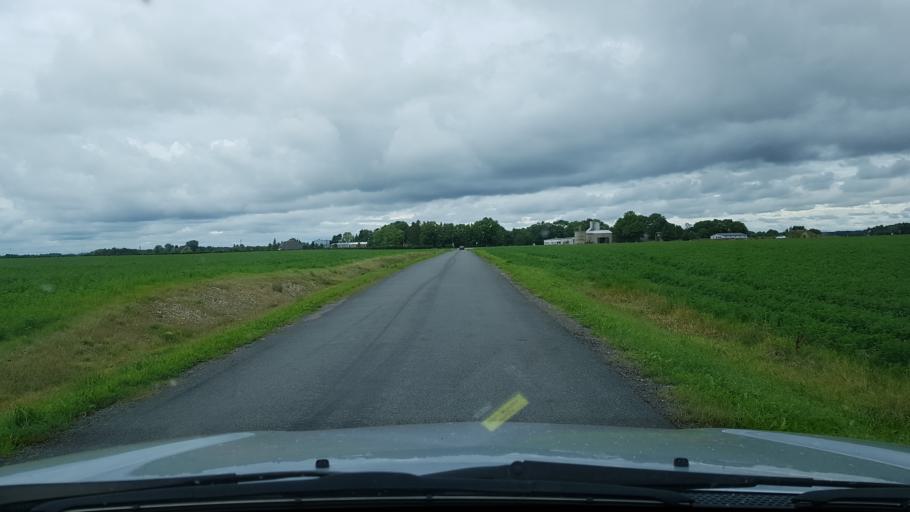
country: EE
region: Harju
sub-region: Rae vald
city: Vaida
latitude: 59.3576
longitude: 24.9650
